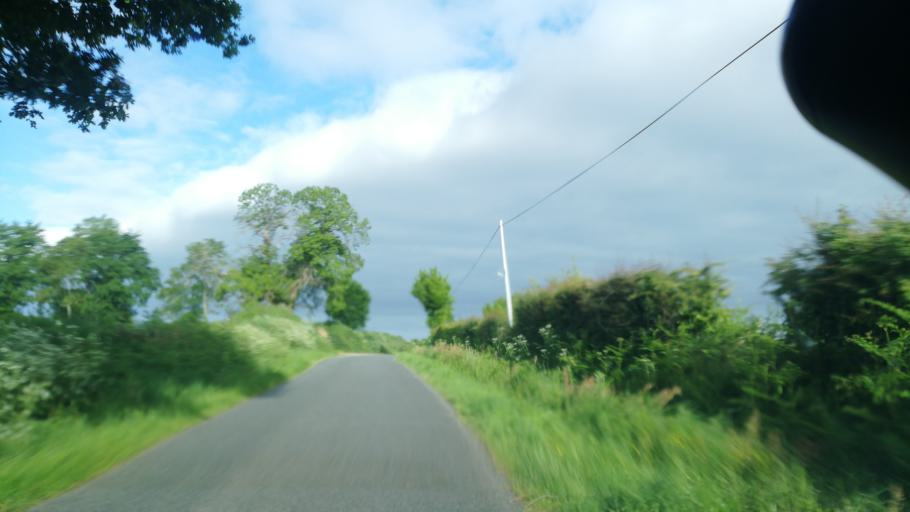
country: FR
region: Poitou-Charentes
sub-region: Departement des Deux-Sevres
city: Moncoutant
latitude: 46.6827
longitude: -0.5684
